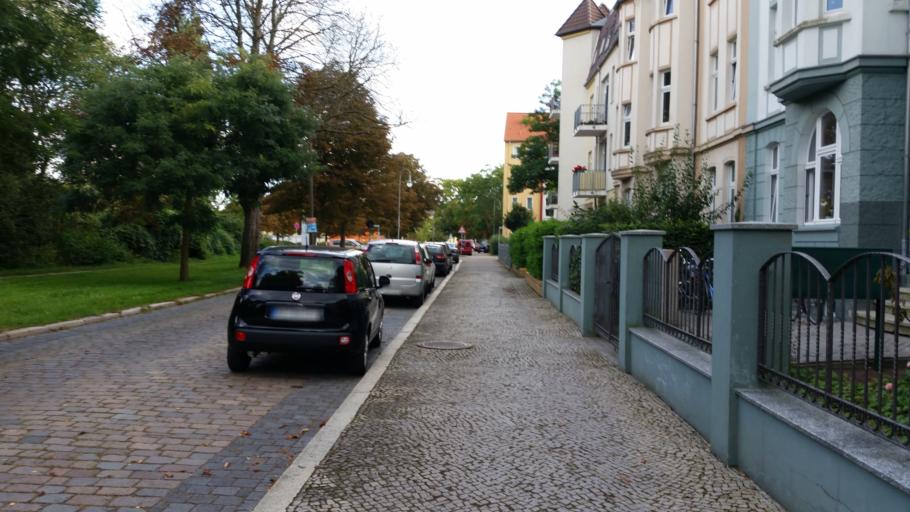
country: DE
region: Saxony-Anhalt
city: Dessau
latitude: 51.8447
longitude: 12.2480
